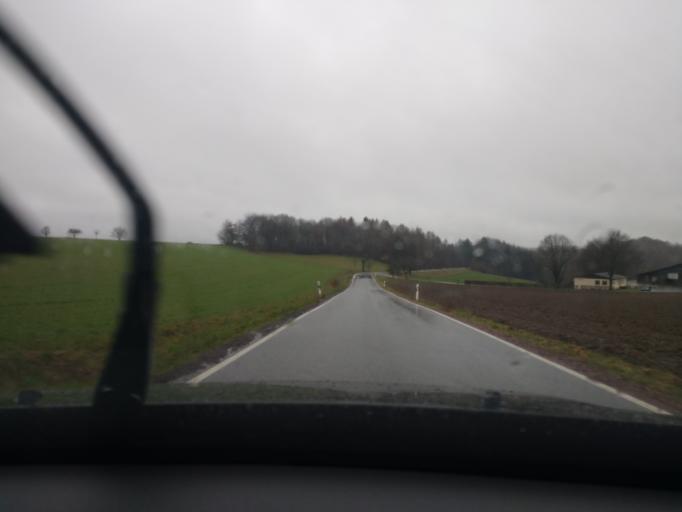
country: DE
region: Rheinland-Pfalz
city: Lampaden
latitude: 49.6519
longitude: 6.6924
